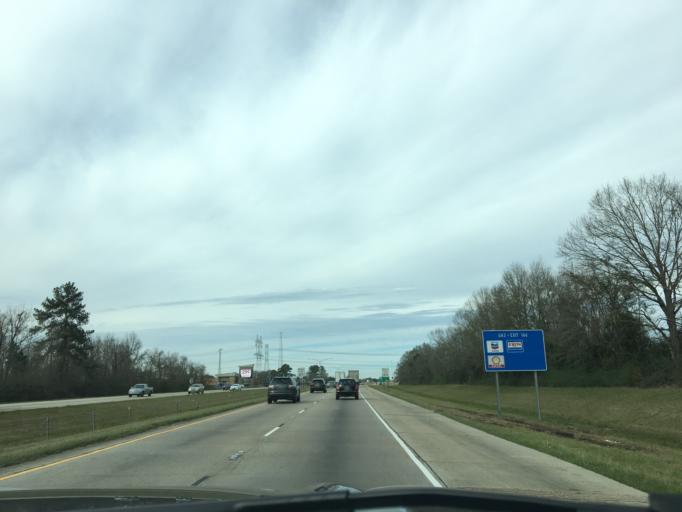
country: US
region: Louisiana
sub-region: East Baton Rouge Parish
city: Old Jefferson
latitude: 30.3391
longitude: -91.0230
